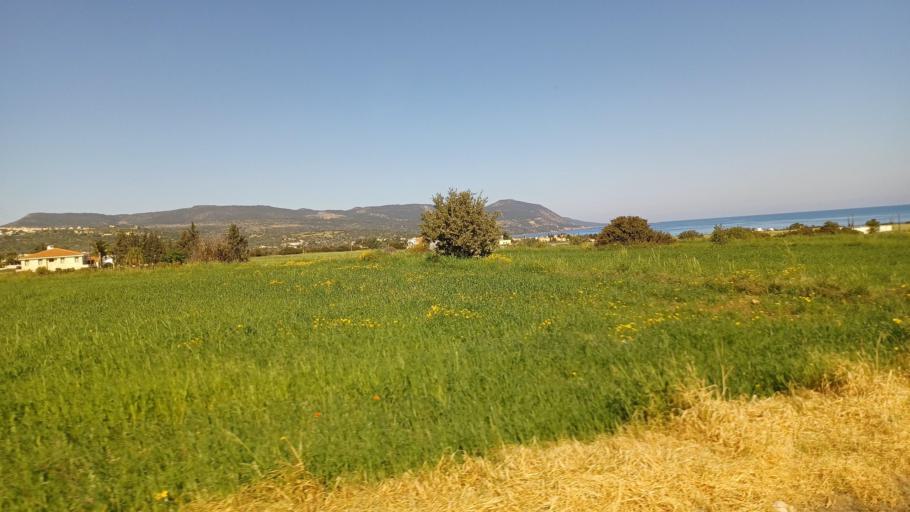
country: CY
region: Pafos
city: Polis
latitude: 35.0356
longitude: 32.3941
